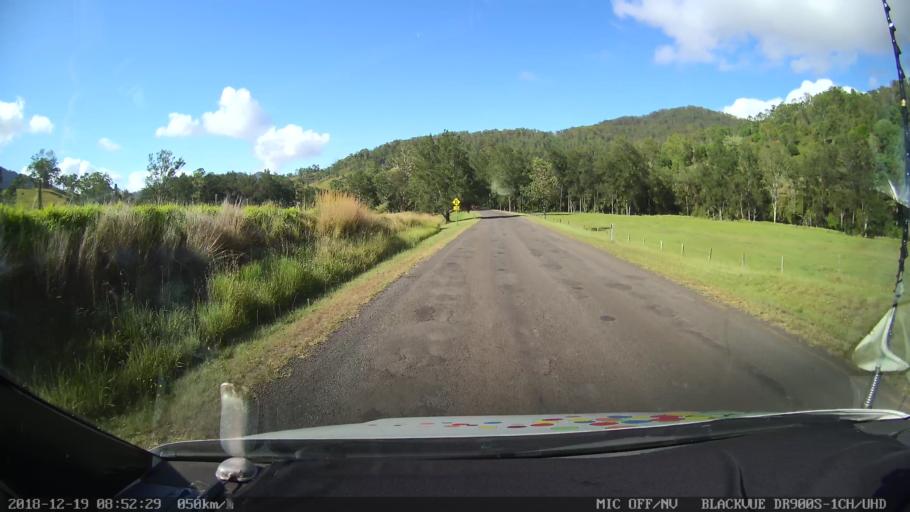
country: AU
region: New South Wales
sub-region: Kyogle
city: Kyogle
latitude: -28.3955
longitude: 152.9773
